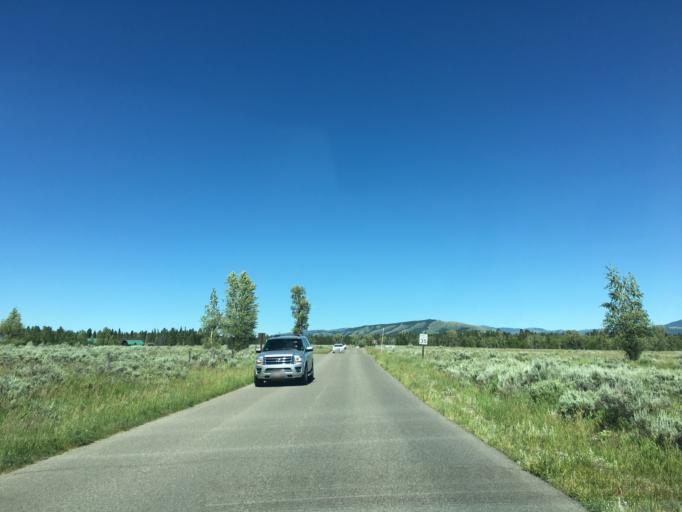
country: US
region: Wyoming
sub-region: Teton County
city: Moose Wilson Road
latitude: 43.5977
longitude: -110.8022
